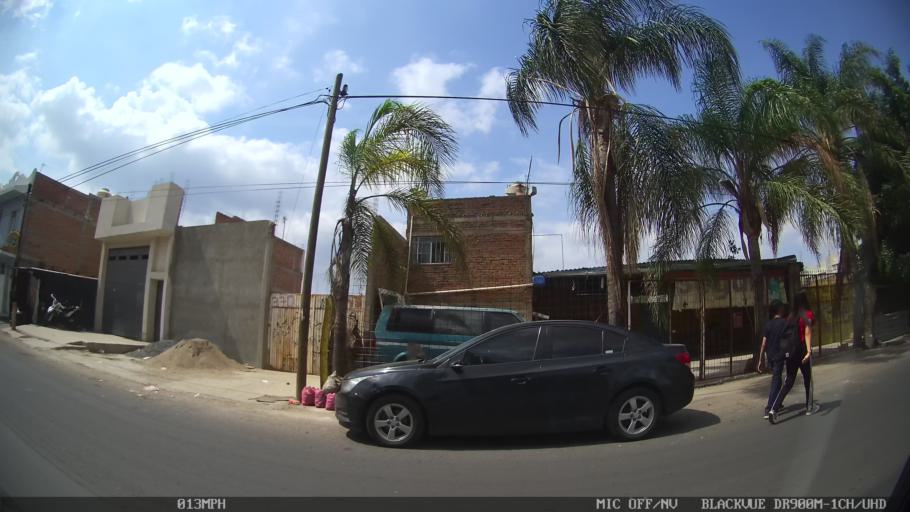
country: MX
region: Jalisco
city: Tonala
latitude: 20.6243
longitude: -103.2299
